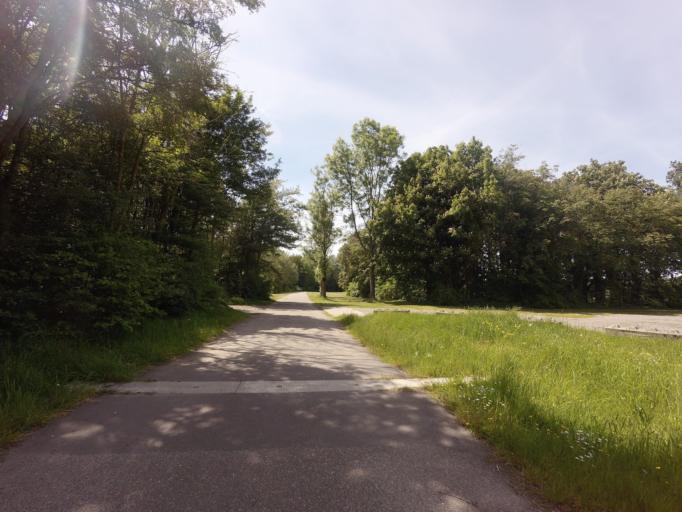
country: NL
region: North Holland
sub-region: Gemeente Zaanstad
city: Zaanstad
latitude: 52.3934
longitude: 4.7482
